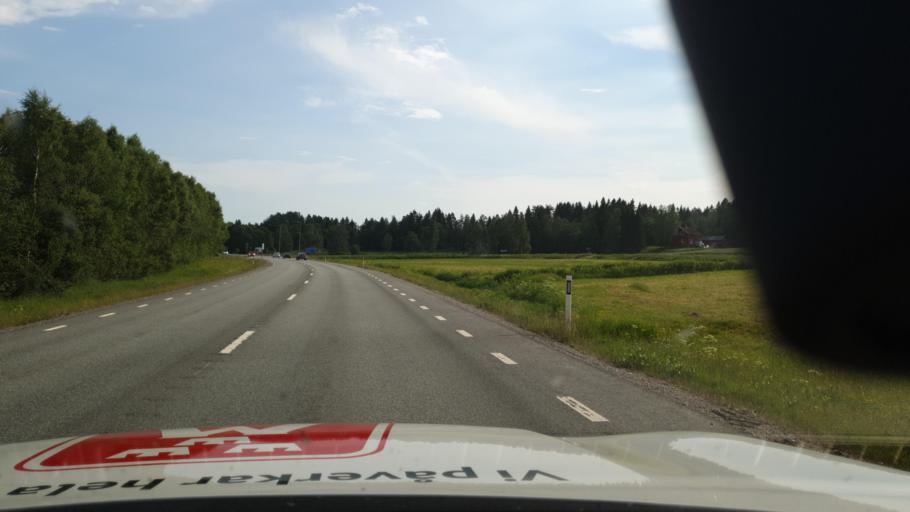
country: SE
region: Vaesterbotten
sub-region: Skelleftea Kommun
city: Burea
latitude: 64.3933
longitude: 21.2991
